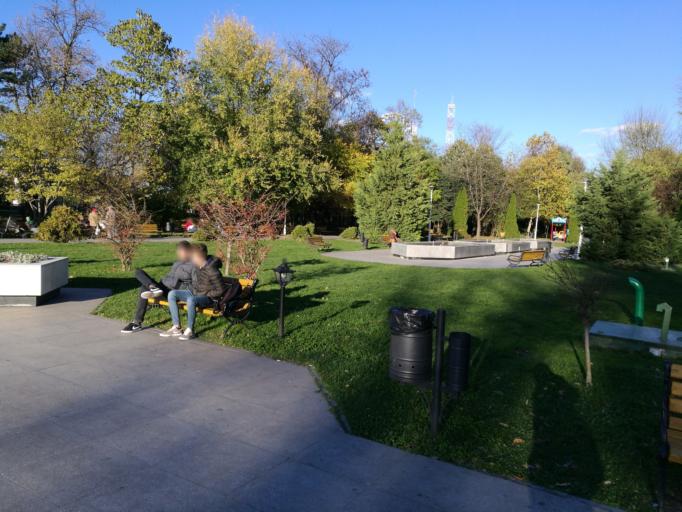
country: RO
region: Bucuresti
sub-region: Municipiul Bucuresti
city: Bucharest
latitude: 44.4643
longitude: 26.1242
